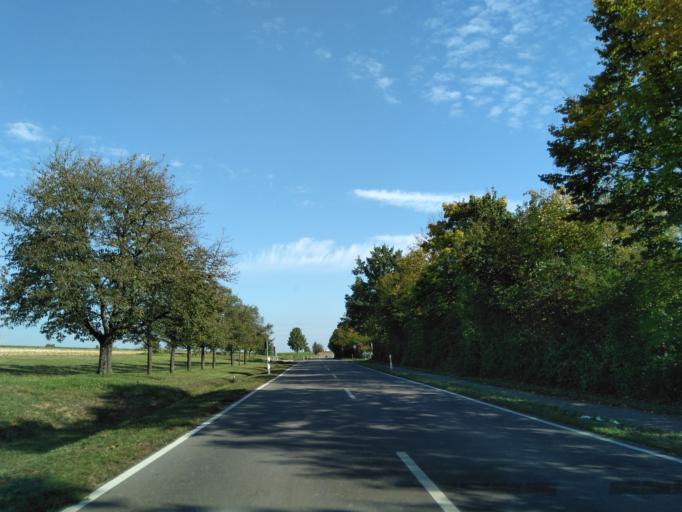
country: DE
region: Baden-Wuerttemberg
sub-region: Regierungsbezirk Stuttgart
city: Bietigheim-Bissingen
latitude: 48.9670
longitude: 9.0813
